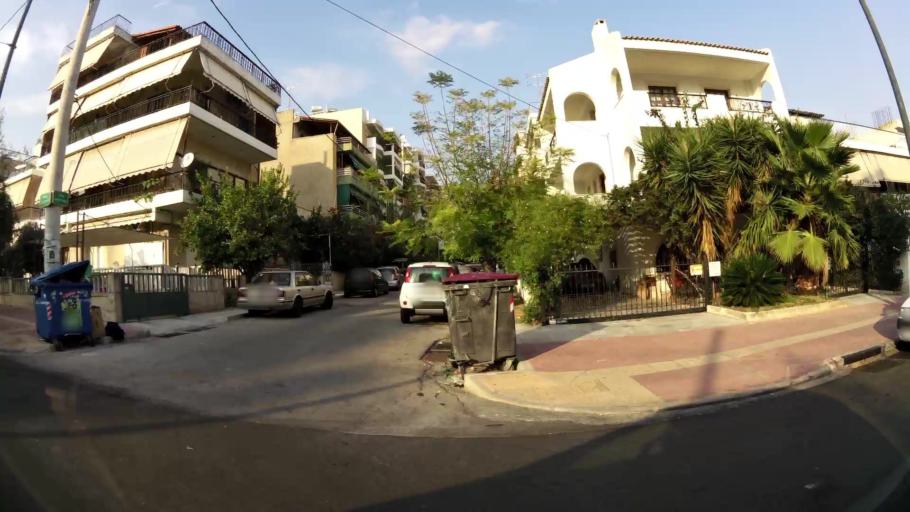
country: GR
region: Attica
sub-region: Nomarchia Athinas
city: Petroupolis
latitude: 38.0396
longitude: 23.6809
